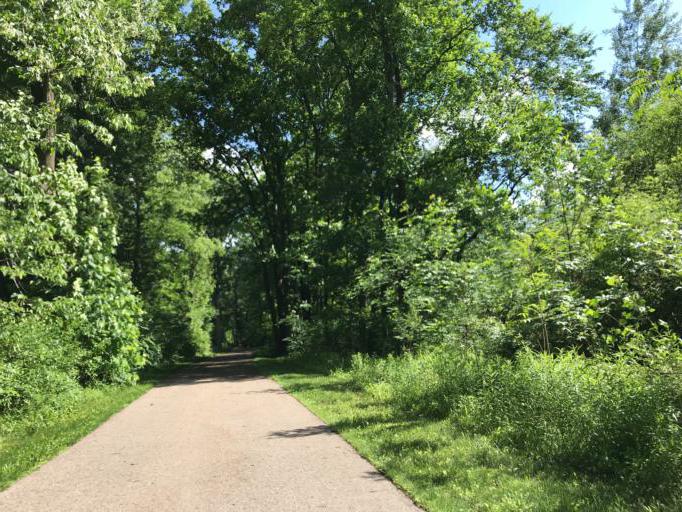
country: US
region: Michigan
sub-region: Oakland County
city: South Lyon
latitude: 42.4364
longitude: -83.6594
